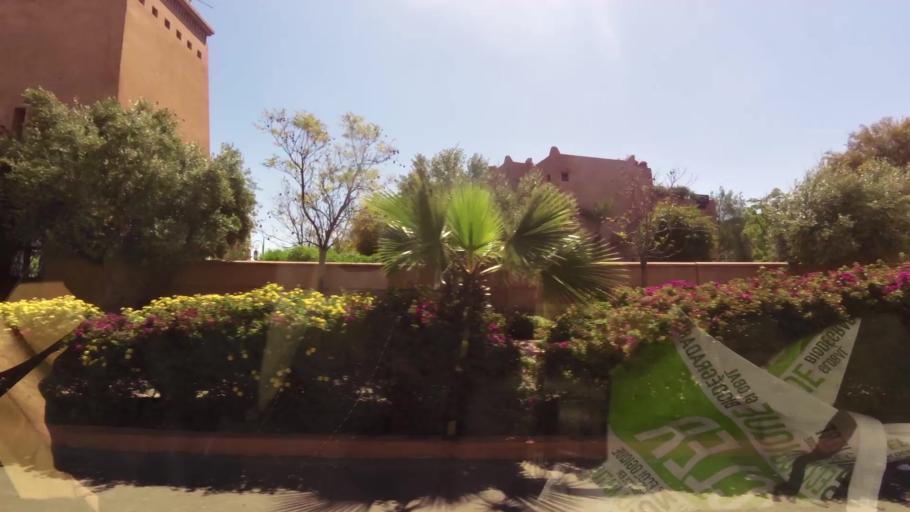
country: MA
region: Marrakech-Tensift-Al Haouz
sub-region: Marrakech
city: Marrakesh
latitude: 31.5993
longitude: -7.9911
